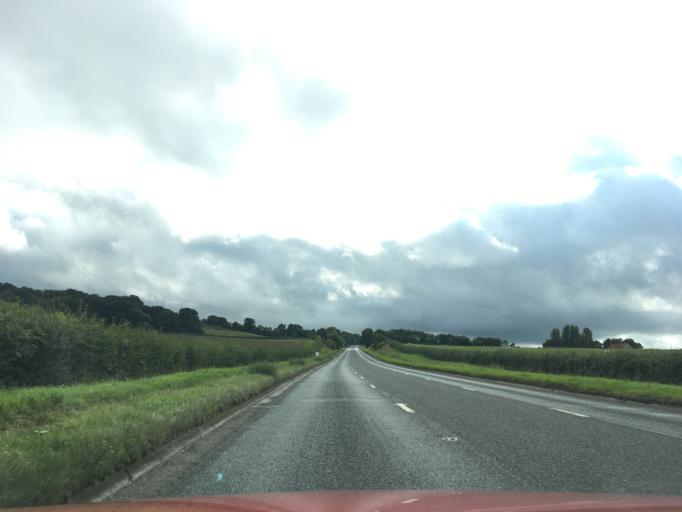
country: GB
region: England
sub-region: South Gloucestershire
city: Tytherington
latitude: 51.6166
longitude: -2.4790
